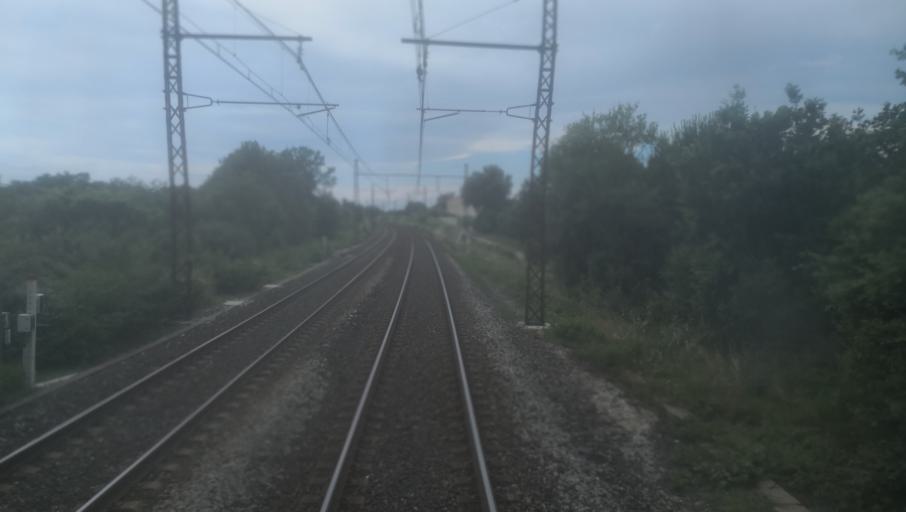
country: FR
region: Languedoc-Roussillon
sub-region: Departement de l'Herault
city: Lunel-Viel
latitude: 43.6783
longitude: 4.0770
